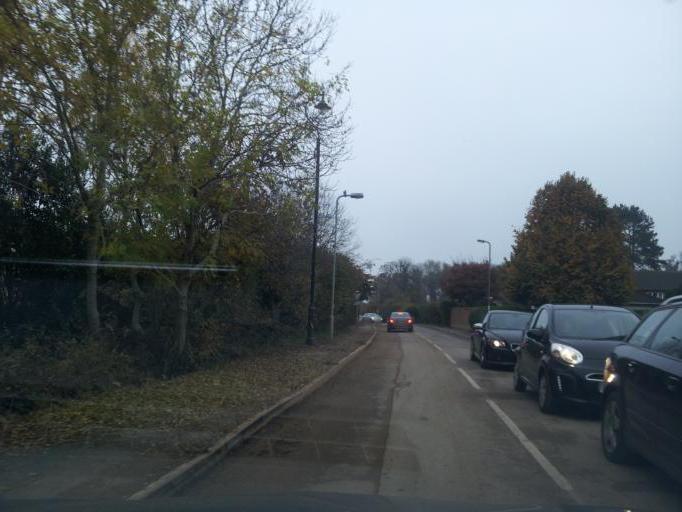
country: GB
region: England
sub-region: Northamptonshire
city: Brackley
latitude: 52.0423
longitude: -1.1446
